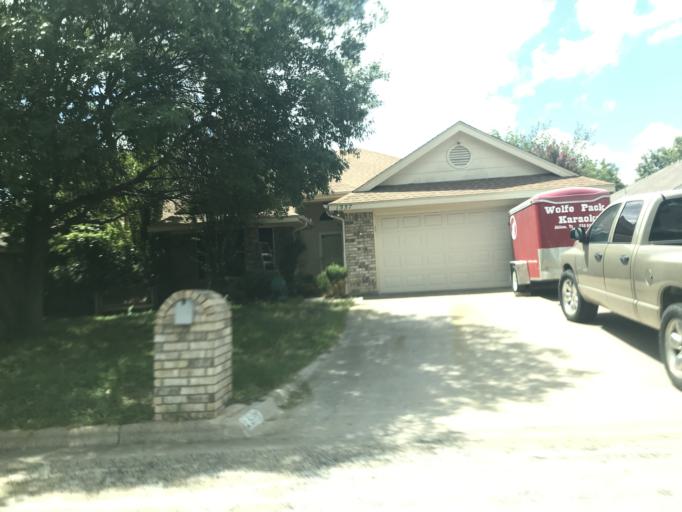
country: US
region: Texas
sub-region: Taylor County
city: Abilene
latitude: 32.4413
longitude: -99.6981
